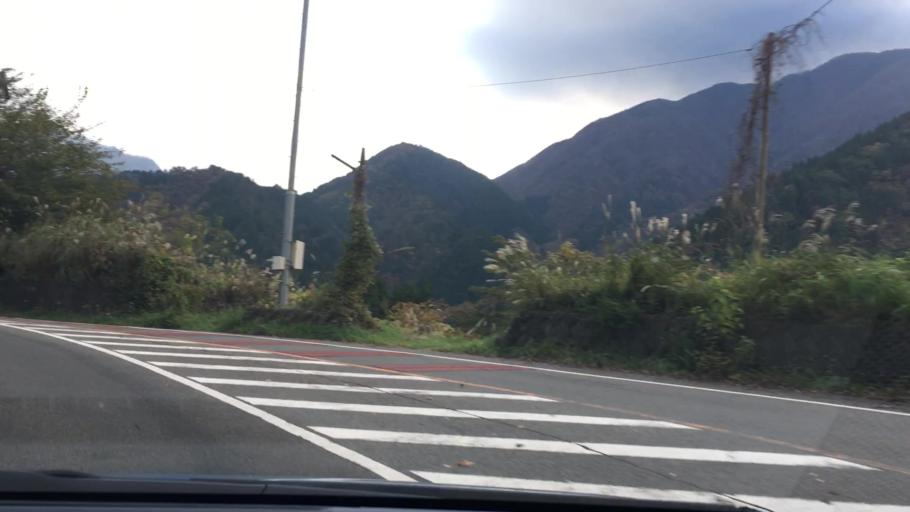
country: JP
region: Yamanashi
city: Uenohara
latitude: 35.5311
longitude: 139.0960
